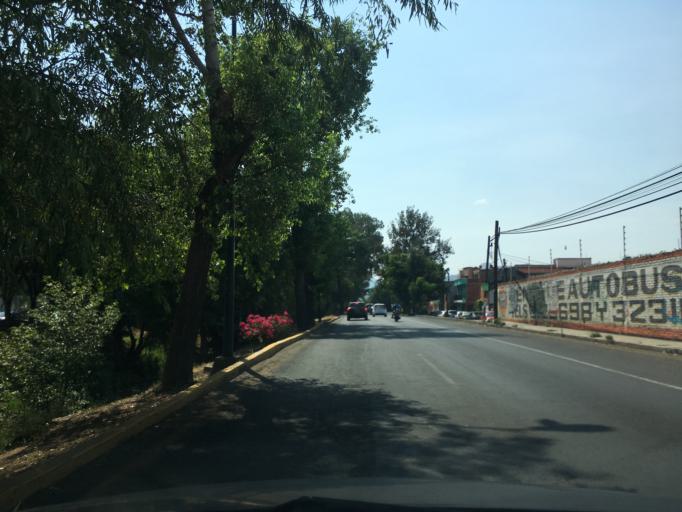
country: MX
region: Michoacan
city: Morelia
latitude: 19.6905
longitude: -101.1896
